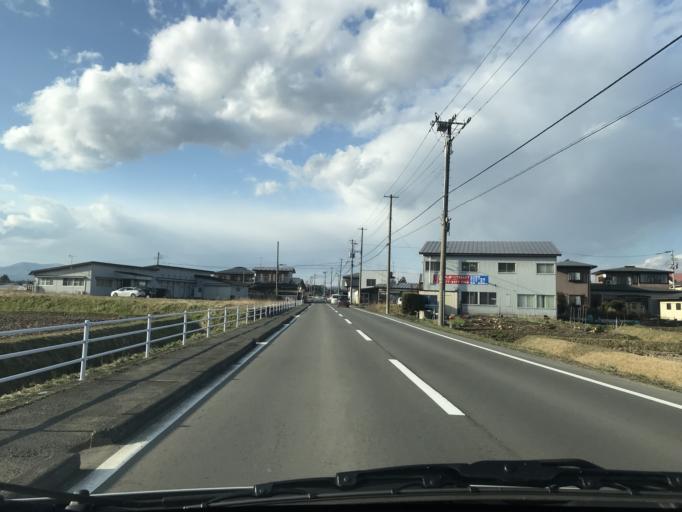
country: JP
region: Iwate
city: Kitakami
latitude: 39.3088
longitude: 141.0708
